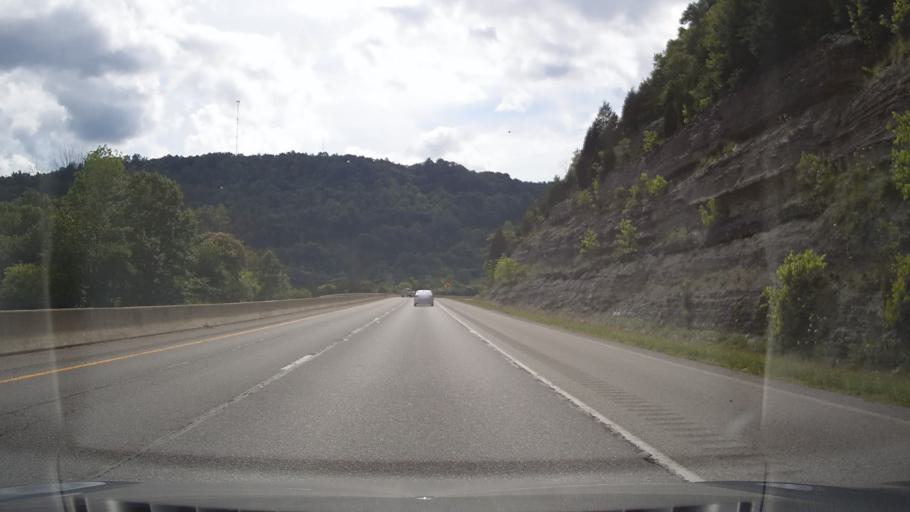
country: US
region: Kentucky
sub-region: Pike County
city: Coal Run Village
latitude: 37.5585
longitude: -82.6388
